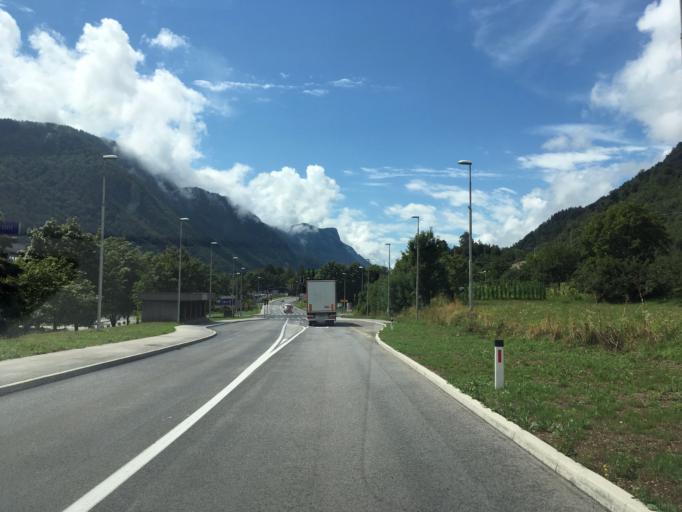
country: SI
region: Jesenice
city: Slovenski Javornik
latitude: 46.4259
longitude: 14.0942
